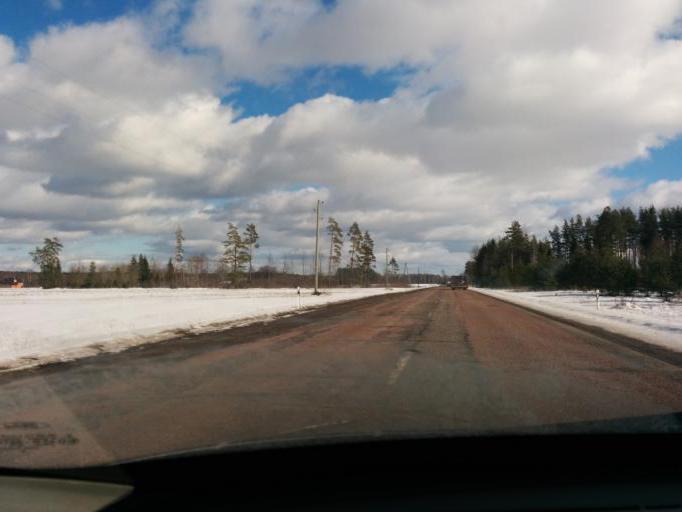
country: LV
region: Cesvaine
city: Cesvaine
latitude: 57.2394
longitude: 26.3693
